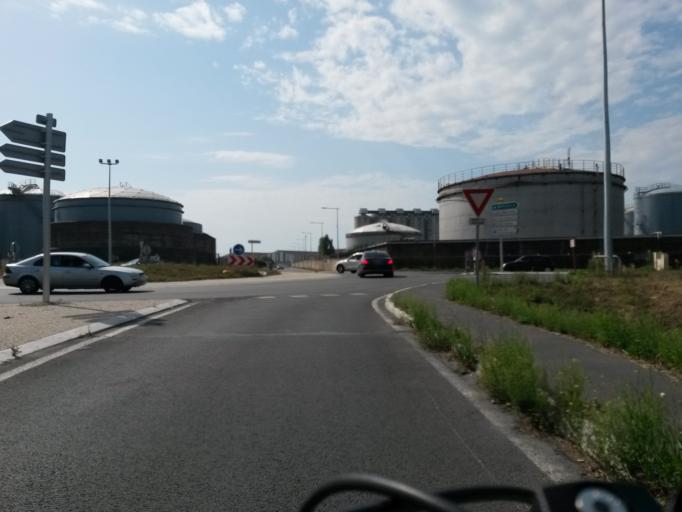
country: FR
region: Poitou-Charentes
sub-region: Departement de la Charente-Maritime
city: Nieul-sur-Mer
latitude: 46.1723
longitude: -1.2130
